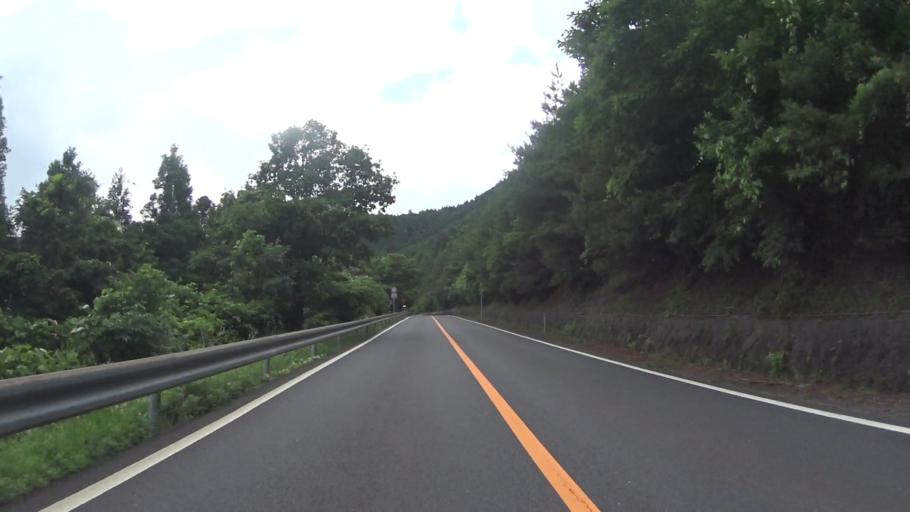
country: JP
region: Oita
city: Tsukawaki
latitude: 33.2056
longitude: 131.2946
